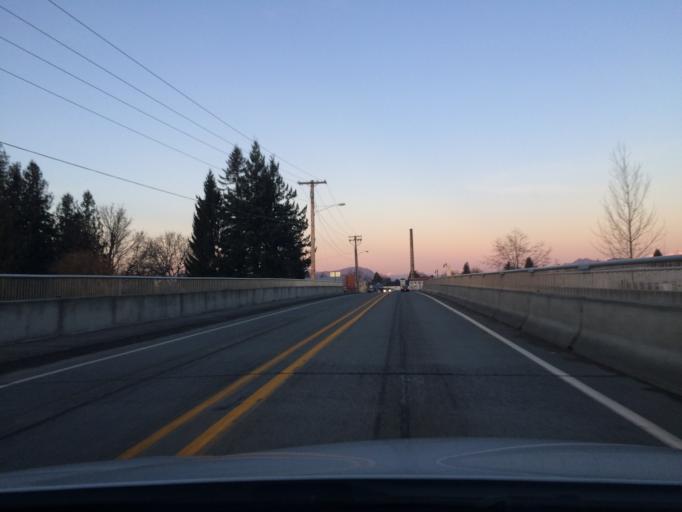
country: US
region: Washington
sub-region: Whatcom County
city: Everson
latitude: 48.9179
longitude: -122.3492
